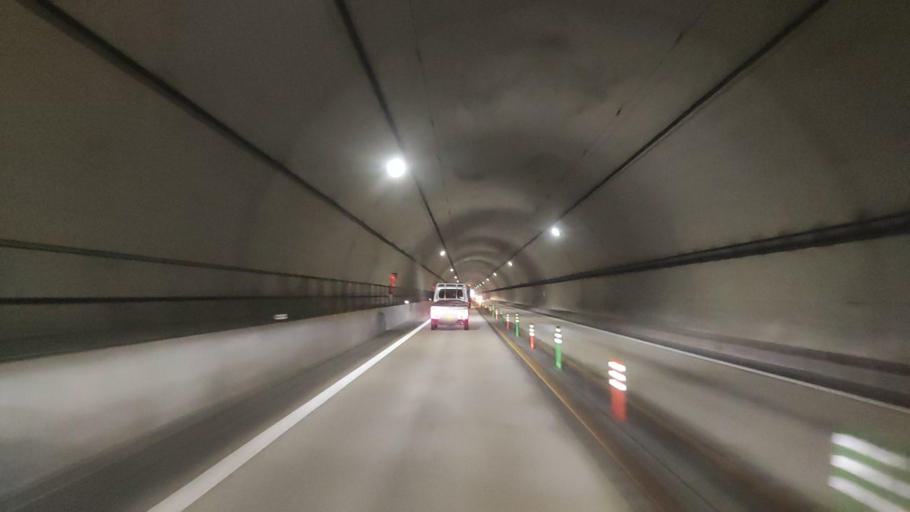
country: JP
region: Wakayama
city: Tanabe
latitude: 33.6073
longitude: 135.4280
